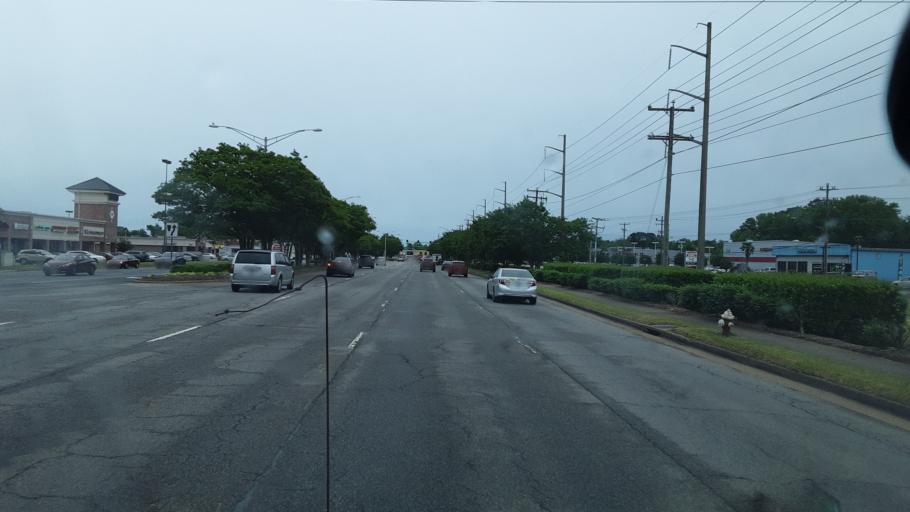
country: US
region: Virginia
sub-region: City of Virginia Beach
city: Virginia Beach
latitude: 36.8396
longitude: -76.1057
